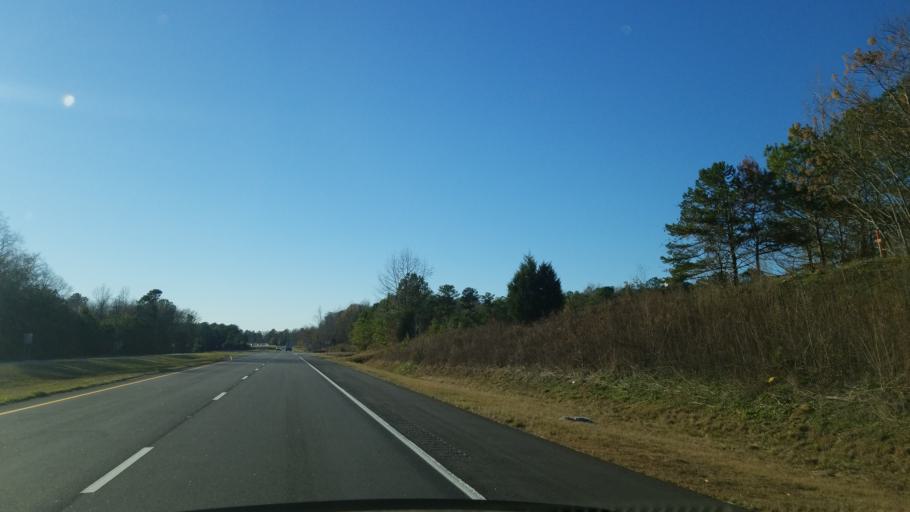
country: US
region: Georgia
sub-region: Talbot County
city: Talbotton
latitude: 32.5752
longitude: -84.5841
